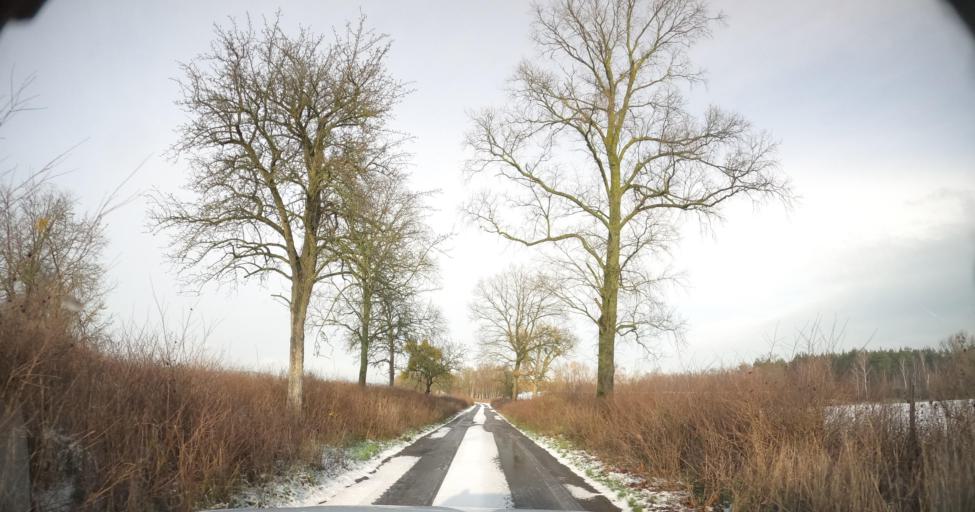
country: PL
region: West Pomeranian Voivodeship
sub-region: Powiat gryfinski
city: Mieszkowice
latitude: 52.7542
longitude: 14.4898
